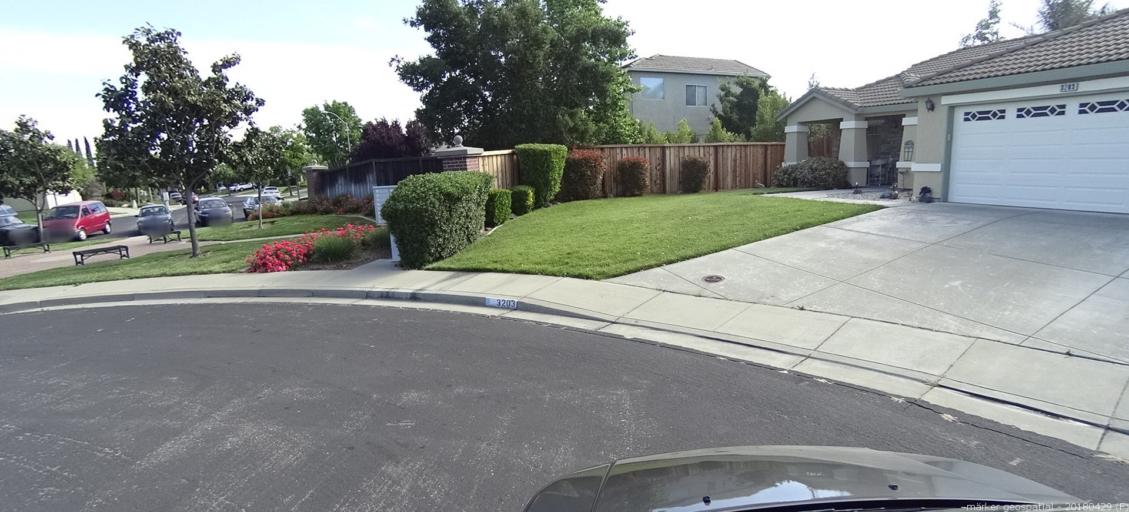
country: US
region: California
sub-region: Yolo County
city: West Sacramento
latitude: 38.5396
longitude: -121.5646
